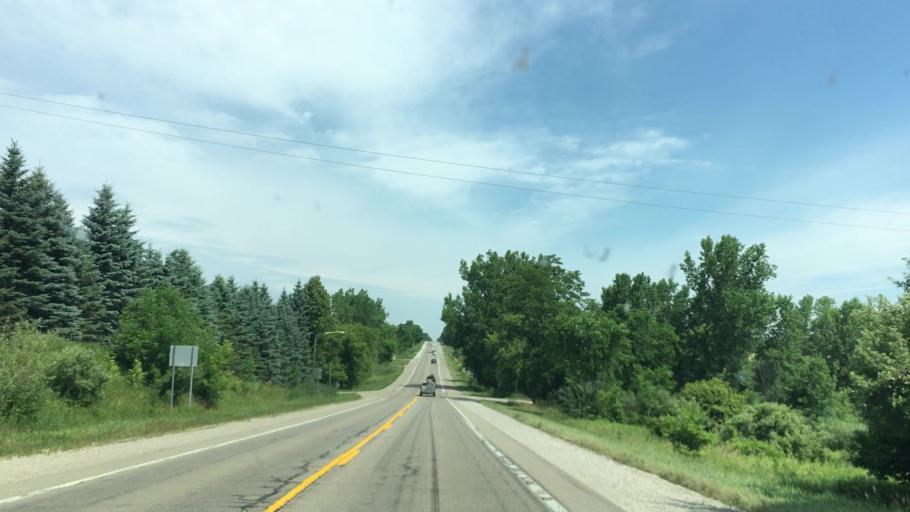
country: US
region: Michigan
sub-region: Lapeer County
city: Imlay City
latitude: 43.1082
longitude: -83.0723
